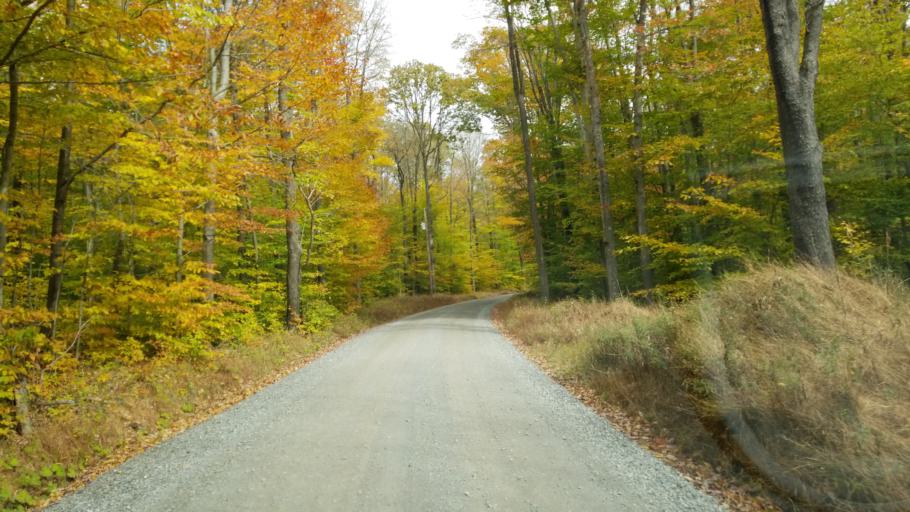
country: US
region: Pennsylvania
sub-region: Clearfield County
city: Clearfield
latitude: 41.1963
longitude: -78.3951
